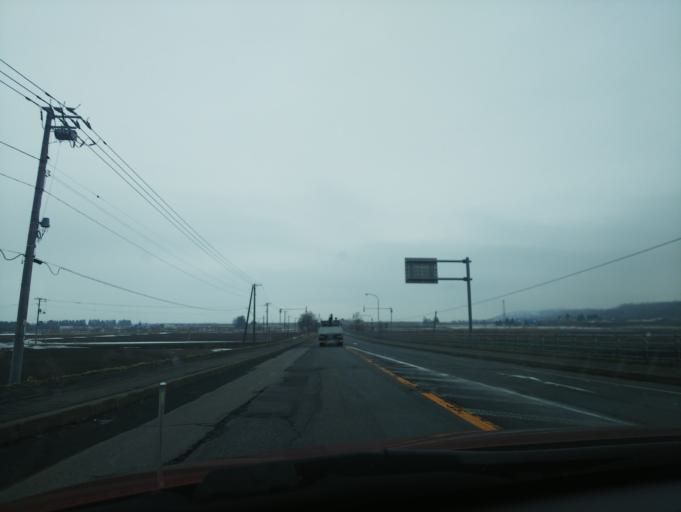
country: JP
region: Hokkaido
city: Nayoro
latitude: 44.0643
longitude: 142.3993
